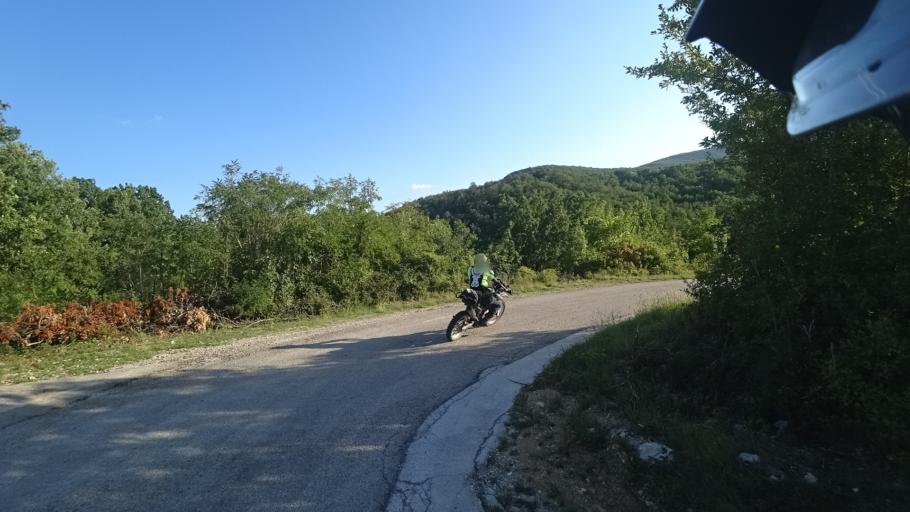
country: HR
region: Sibensko-Kniniska
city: Knin
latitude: 44.1015
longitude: 16.1577
